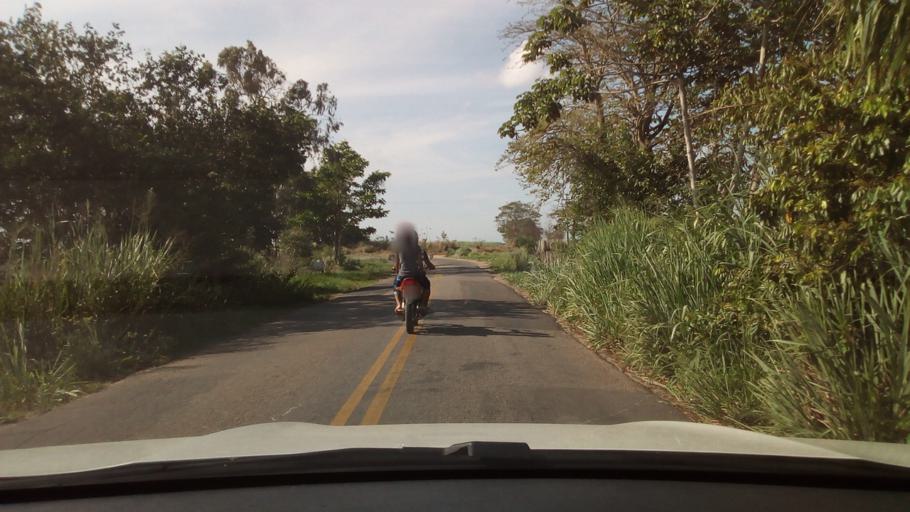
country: BR
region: Rio Grande do Norte
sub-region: Ares
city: Ares
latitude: -6.2386
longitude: -35.1726
